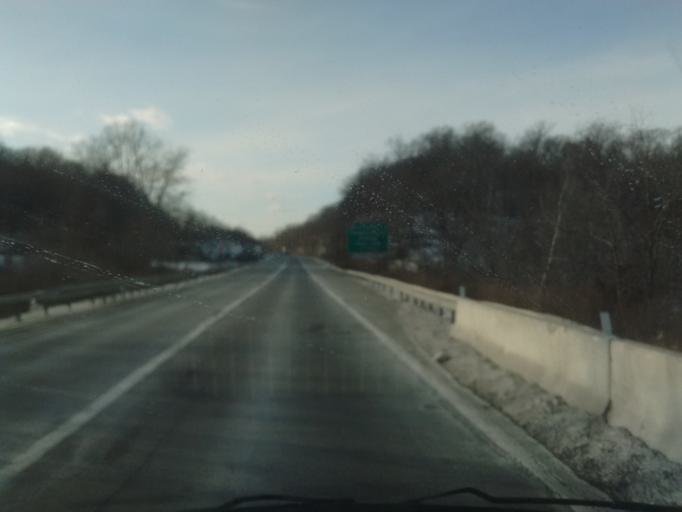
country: US
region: New York
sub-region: Dutchess County
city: Hillside Lake
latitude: 41.5485
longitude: -73.7334
